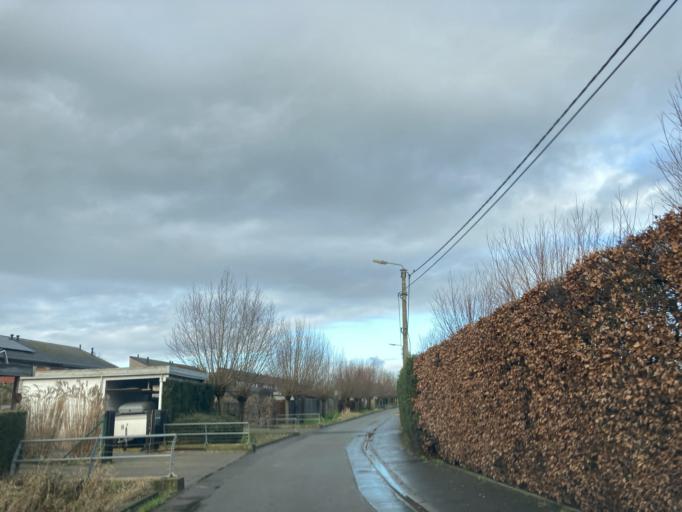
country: BE
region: Flanders
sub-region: Provincie West-Vlaanderen
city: Tielt
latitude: 51.0327
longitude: 3.3422
